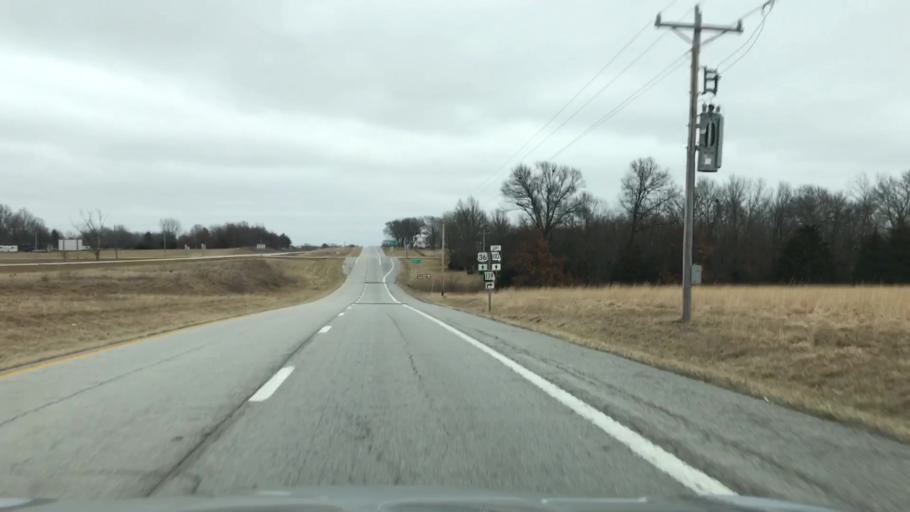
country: US
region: Missouri
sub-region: Linn County
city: Linneus
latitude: 39.7783
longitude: -93.1788
